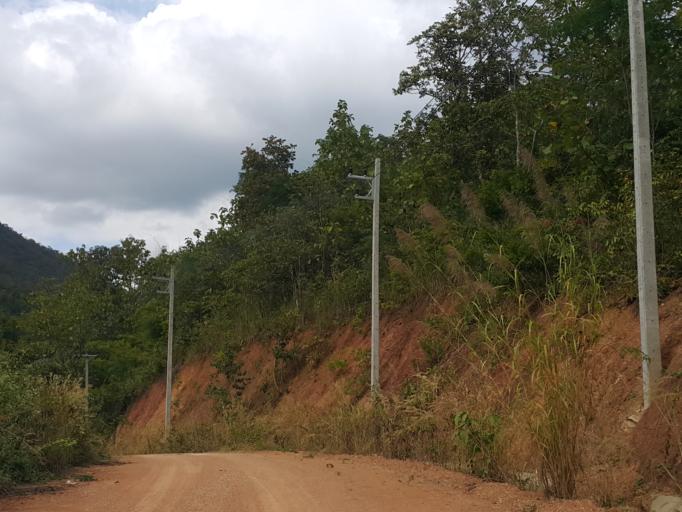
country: TH
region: Lampang
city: Chae Hom
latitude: 18.5750
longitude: 99.4431
